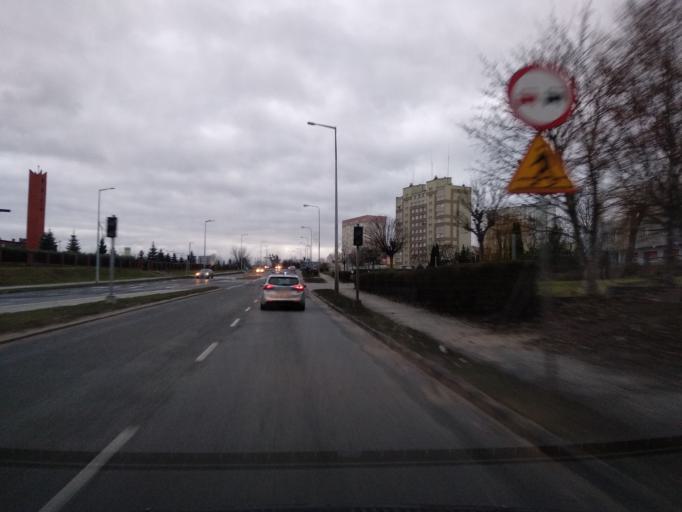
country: PL
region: Greater Poland Voivodeship
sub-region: Konin
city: Konin
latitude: 52.2342
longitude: 18.2687
